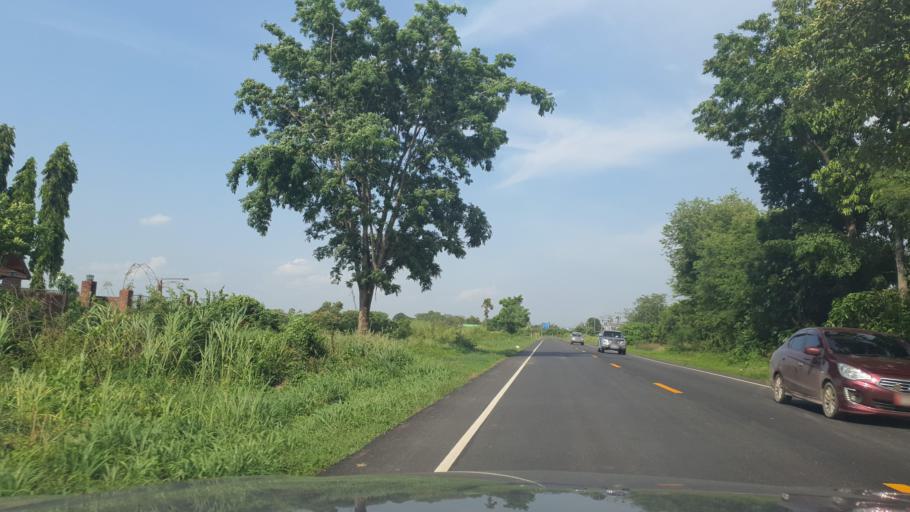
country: TH
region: Sukhothai
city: Si Samrong
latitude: 17.1714
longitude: 99.8453
